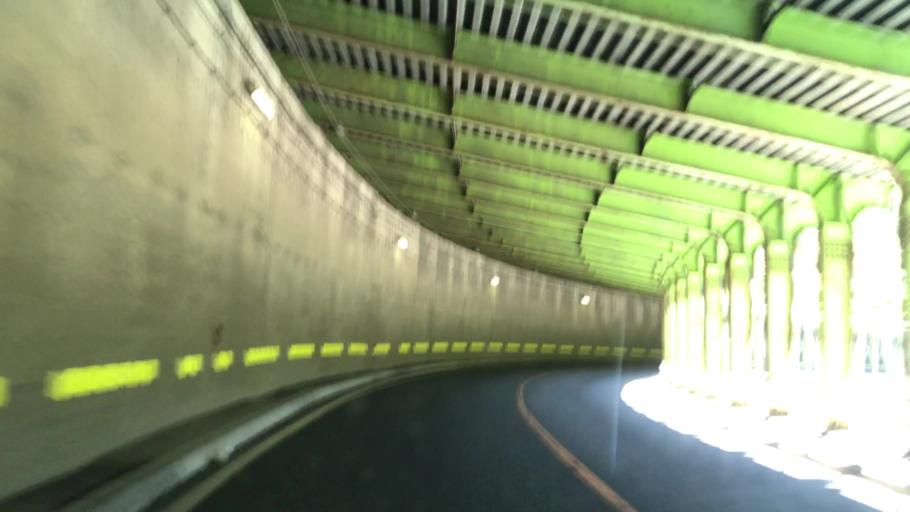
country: JP
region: Hokkaido
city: Shimo-furano
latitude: 42.9636
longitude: 142.6232
